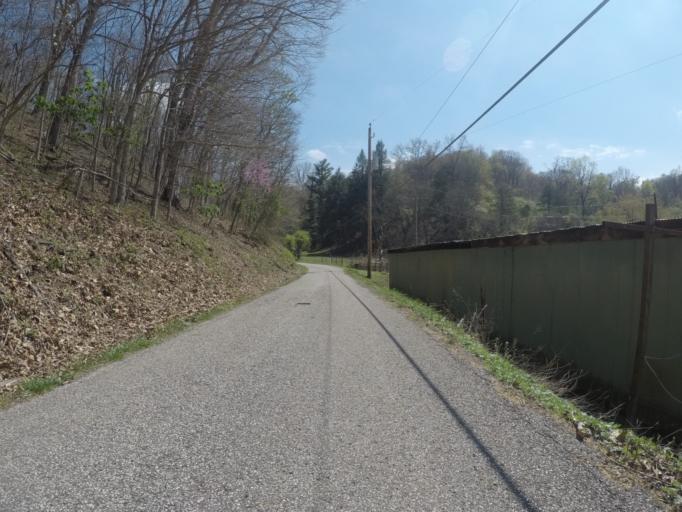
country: US
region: Ohio
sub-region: Lawrence County
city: Burlington
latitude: 38.3922
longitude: -82.5260
